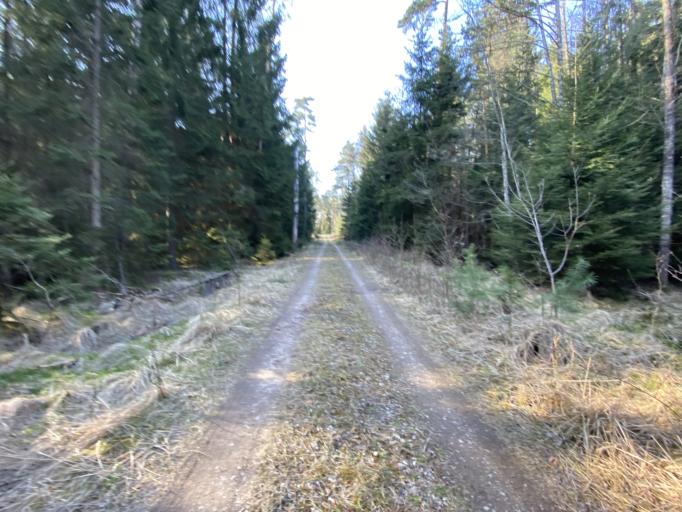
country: DE
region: Bavaria
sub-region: Regierungsbezirk Mittelfranken
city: Buckenhof
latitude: 49.5523
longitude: 11.0681
